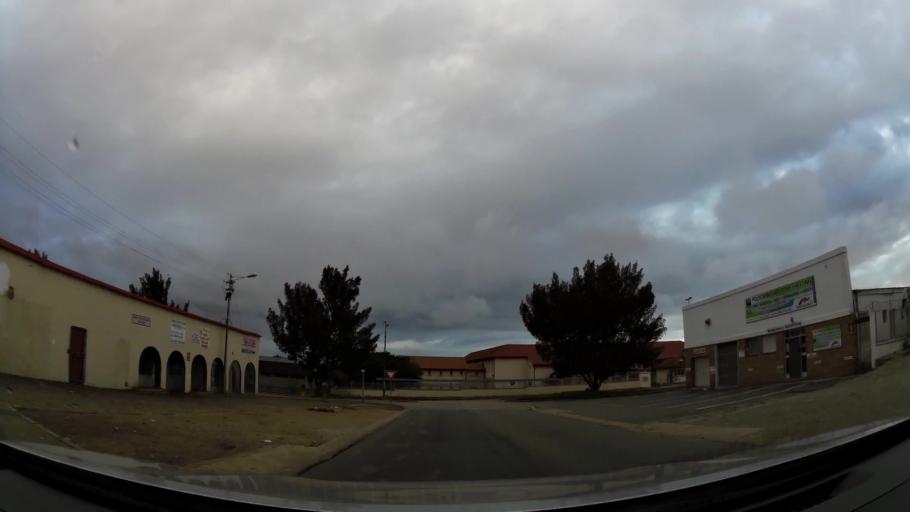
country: ZA
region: Eastern Cape
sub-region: Nelson Mandela Bay Metropolitan Municipality
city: Port Elizabeth
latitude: -33.9210
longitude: 25.5938
